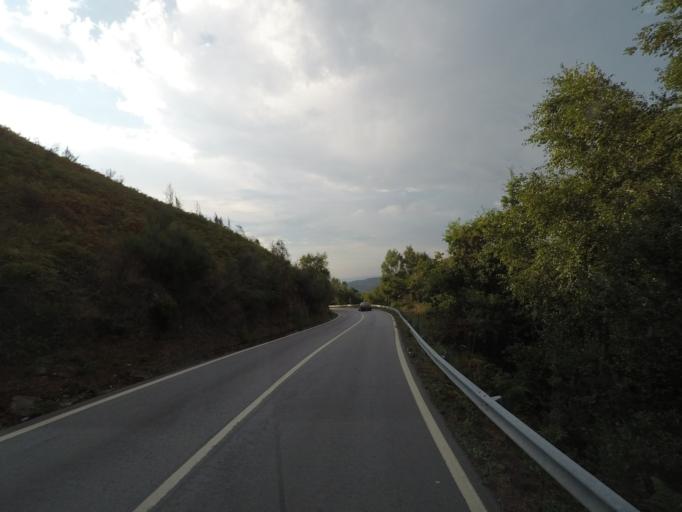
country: PT
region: Porto
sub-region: Baiao
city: Valadares
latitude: 41.1987
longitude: -7.9535
